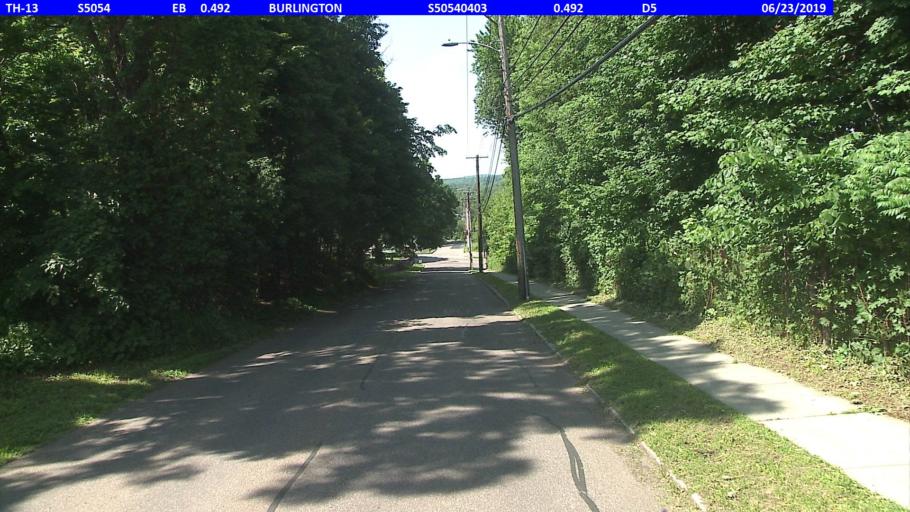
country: US
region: Vermont
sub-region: Chittenden County
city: Burlington
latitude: 44.4877
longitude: -73.2021
